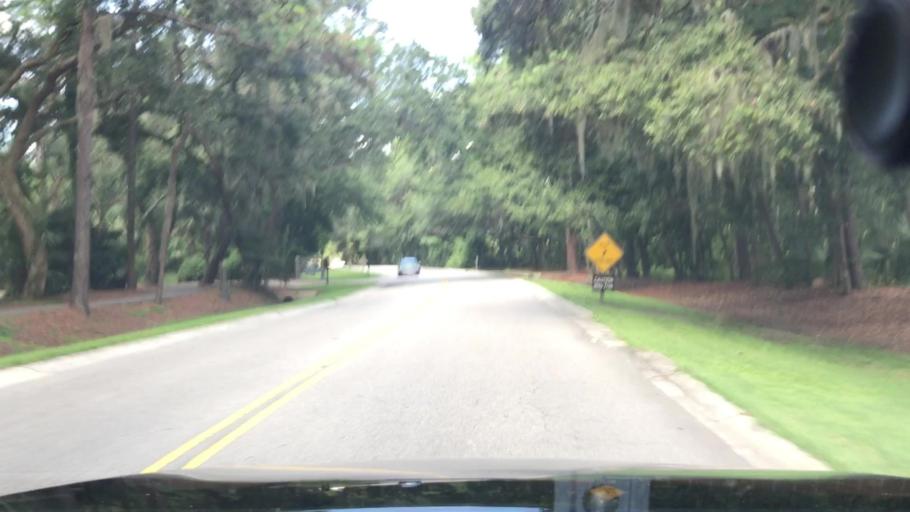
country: US
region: South Carolina
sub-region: Beaufort County
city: Hilton Head Island
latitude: 32.1470
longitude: -80.7816
